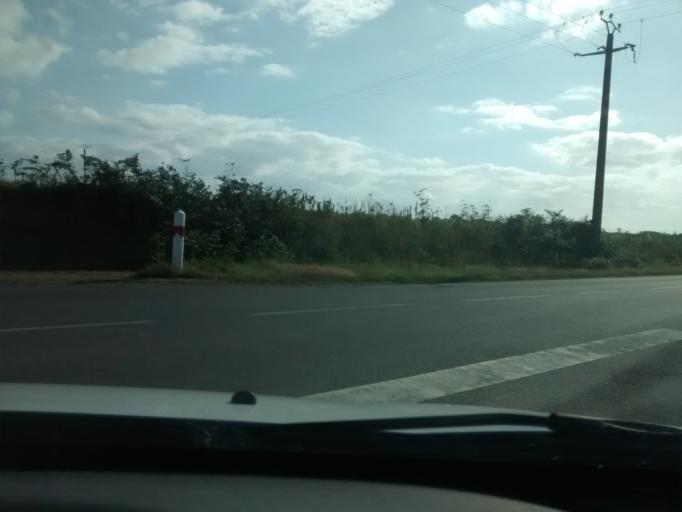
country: FR
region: Brittany
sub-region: Departement des Cotes-d'Armor
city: Penvenan
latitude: 48.7962
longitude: -3.3021
